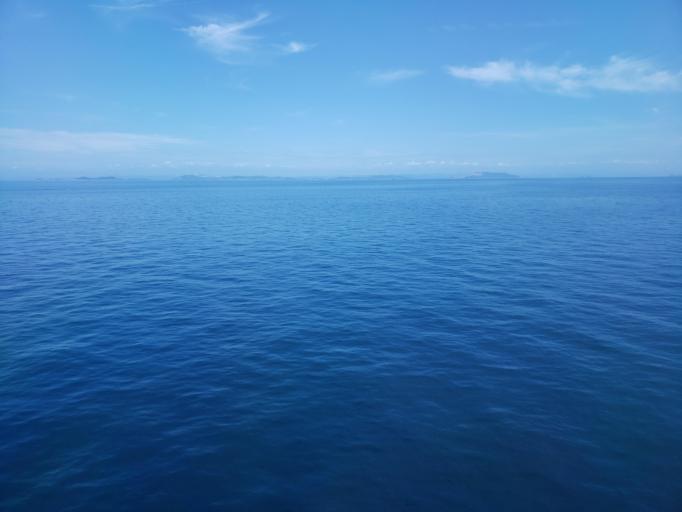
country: JP
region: Hyogo
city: Fukura
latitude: 34.5024
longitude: 134.5953
